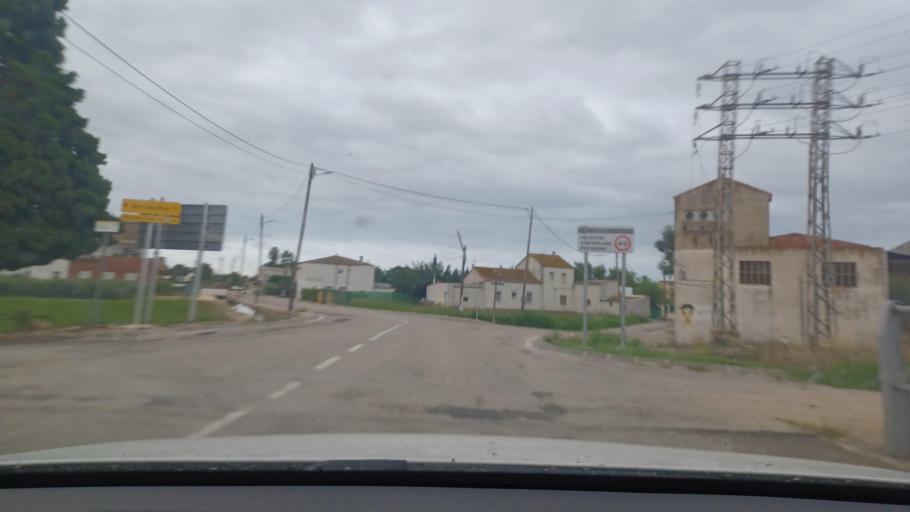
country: ES
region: Catalonia
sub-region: Provincia de Tarragona
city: Deltebre
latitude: 40.7277
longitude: 0.6787
